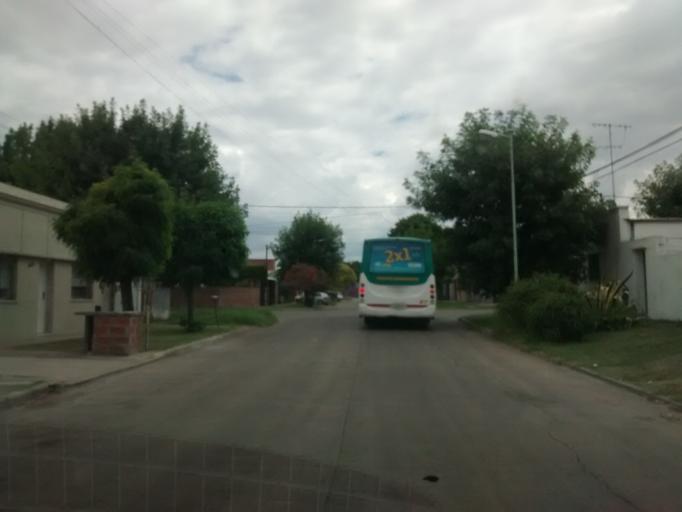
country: AR
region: Buenos Aires
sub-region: Partido de La Plata
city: La Plata
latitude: -34.9372
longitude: -57.9305
